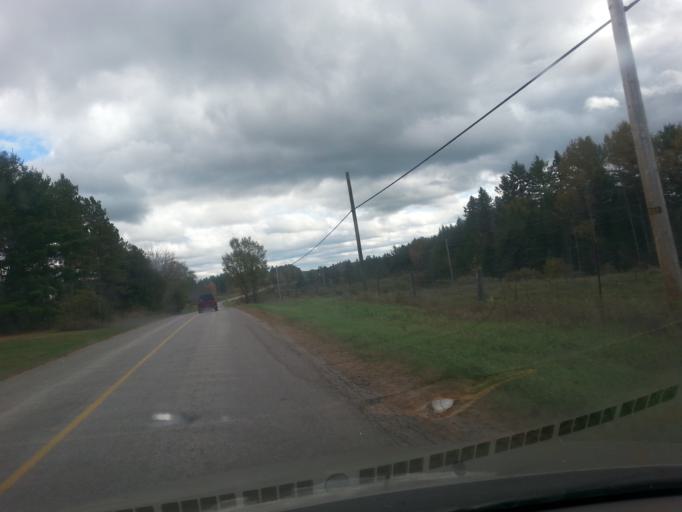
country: CA
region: Ontario
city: Pembroke
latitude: 45.5201
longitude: -77.0608
